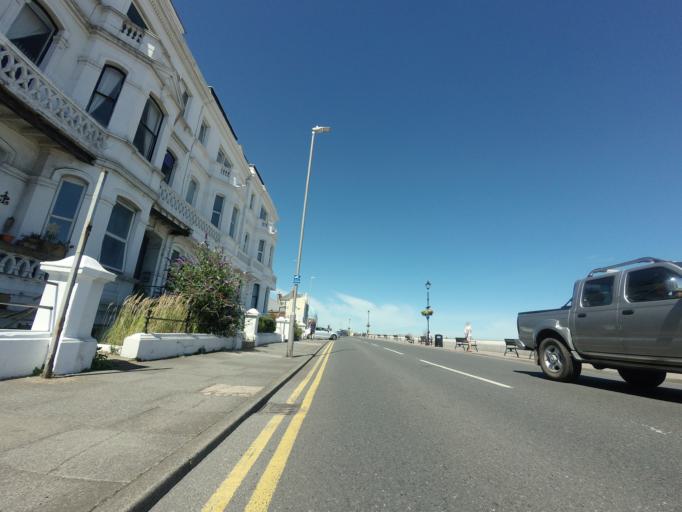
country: GB
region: England
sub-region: Kent
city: Deal
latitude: 51.2216
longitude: 1.4044
